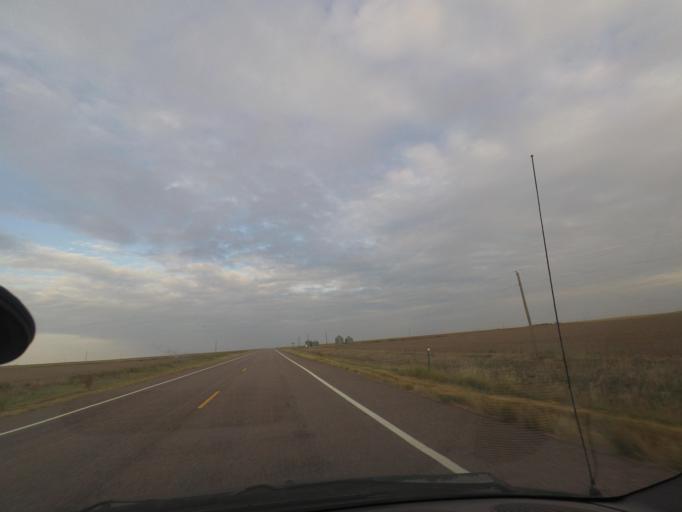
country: US
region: Colorado
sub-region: Yuma County
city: Wray
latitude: 39.7460
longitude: -102.1666
